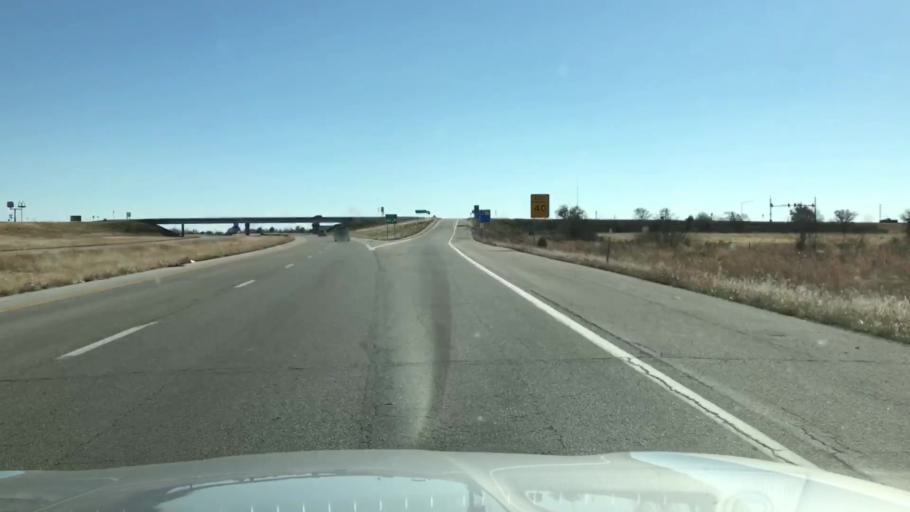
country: US
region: Missouri
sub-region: Jasper County
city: Carthage
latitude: 37.1431
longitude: -94.3252
